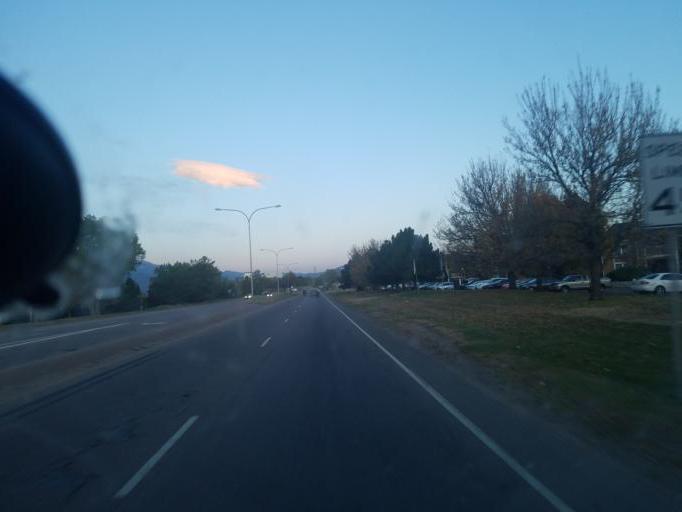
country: US
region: Colorado
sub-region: El Paso County
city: Stratmoor
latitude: 38.8122
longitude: -104.7490
